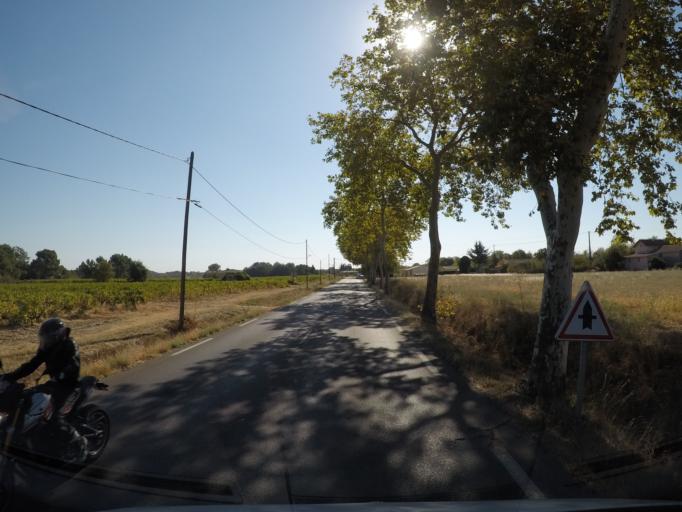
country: FR
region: Languedoc-Roussillon
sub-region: Departement du Gard
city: Boisset-et-Gaujac
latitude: 44.0347
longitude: 4.0060
